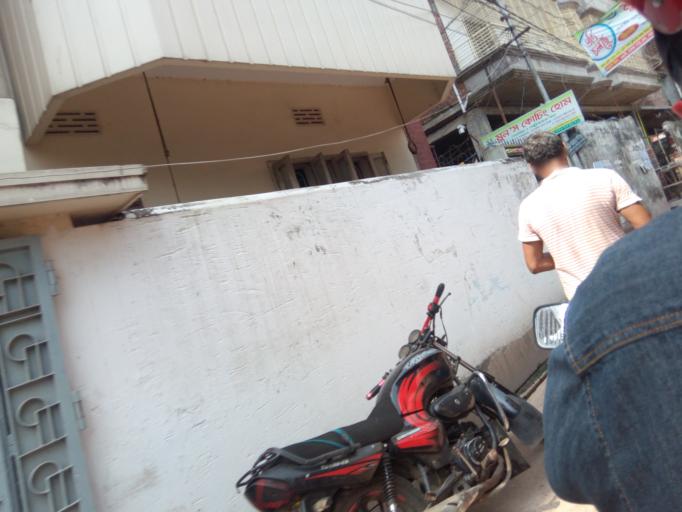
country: BD
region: Dhaka
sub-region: Dhaka
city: Dhaka
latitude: 23.7007
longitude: 90.4247
